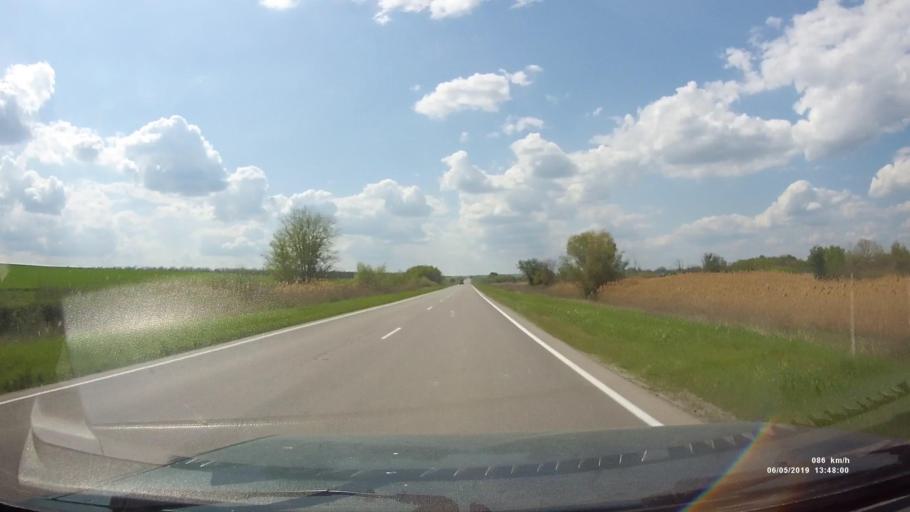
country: RU
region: Rostov
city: Melikhovskaya
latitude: 47.6580
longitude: 40.5523
